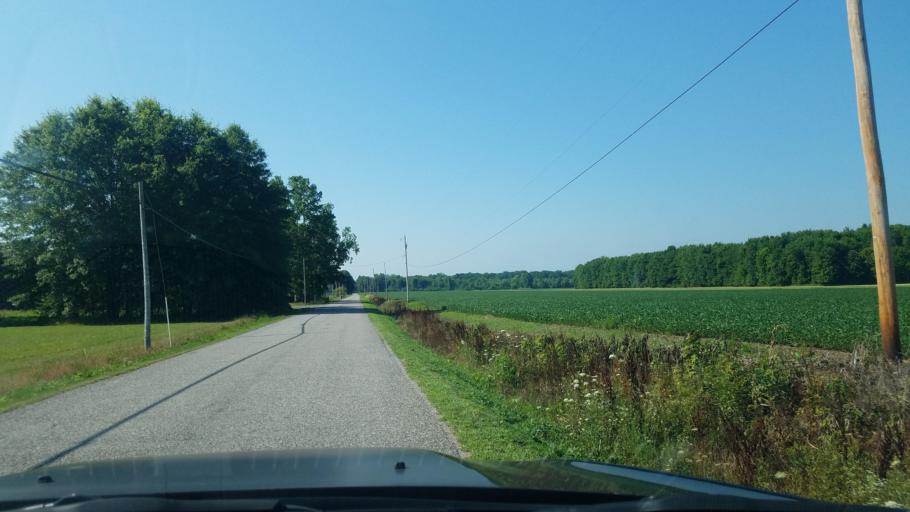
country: US
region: Ohio
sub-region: Trumbull County
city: Leavittsburg
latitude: 41.2703
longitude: -80.9249
